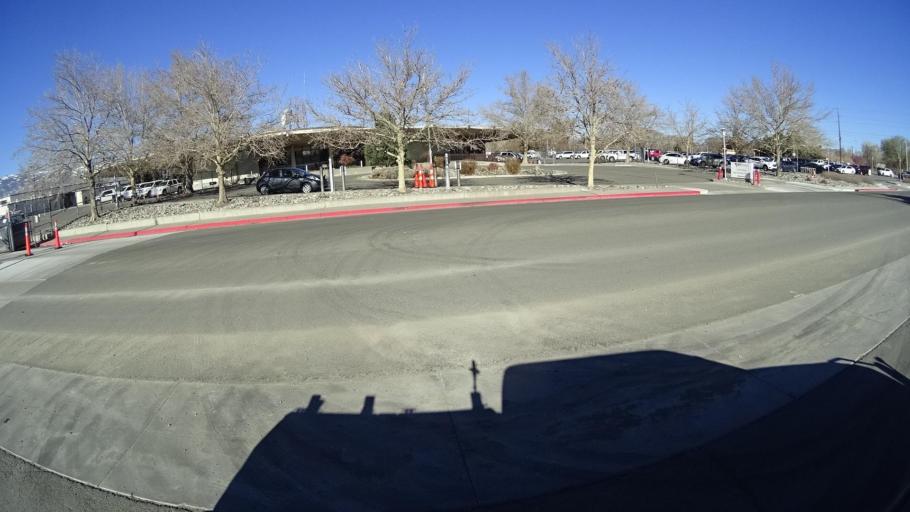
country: US
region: Nevada
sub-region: Washoe County
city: Sparks
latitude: 39.5135
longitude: -119.7554
